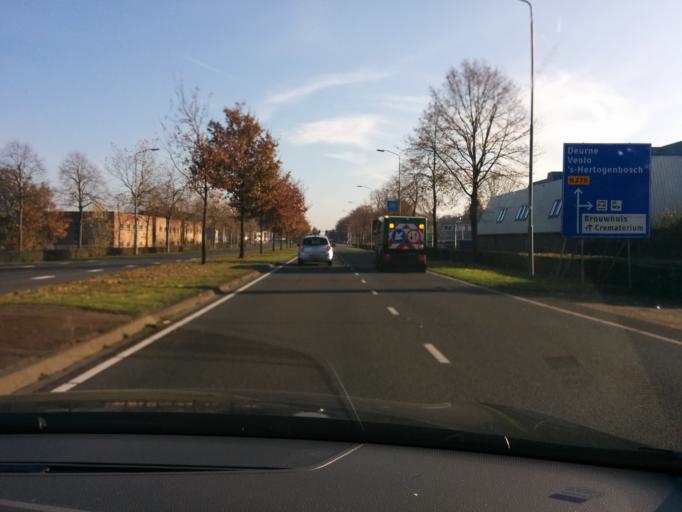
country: NL
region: North Brabant
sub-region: Gemeente Helmond
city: Helmond
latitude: 51.4720
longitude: 5.7015
